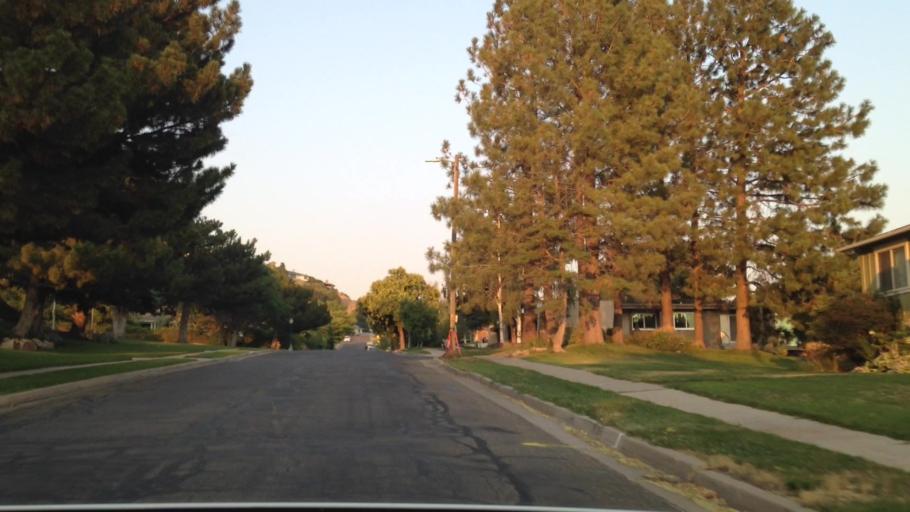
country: US
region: Utah
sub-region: Salt Lake County
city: Salt Lake City
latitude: 40.7890
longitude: -111.8721
